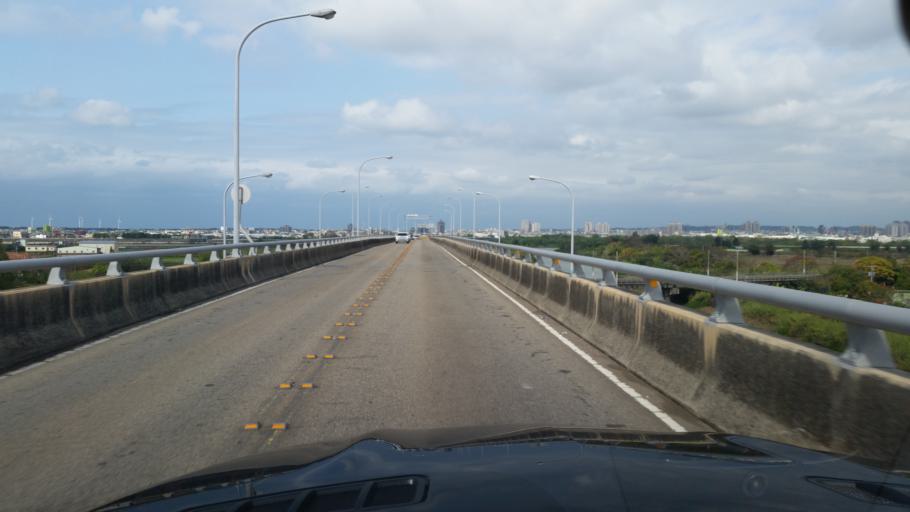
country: TW
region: Taiwan
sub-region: Miaoli
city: Miaoli
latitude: 24.6576
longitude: 120.8670
